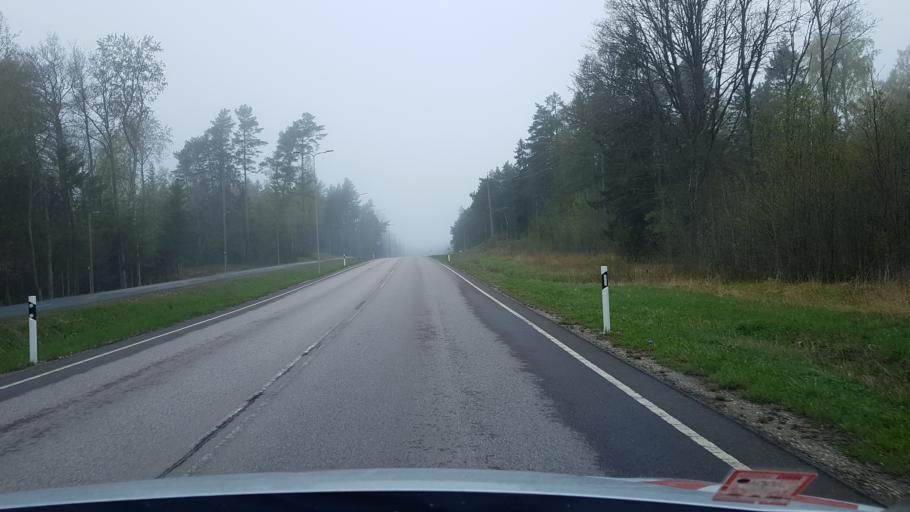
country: EE
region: Harju
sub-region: Viimsi vald
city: Viimsi
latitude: 59.5164
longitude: 24.9006
